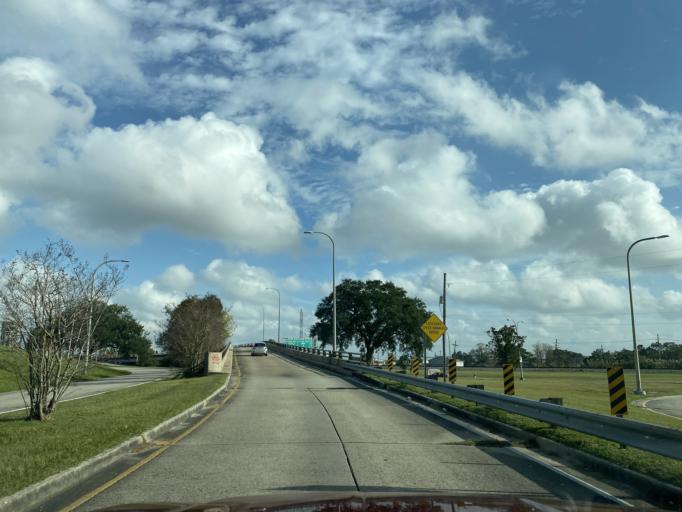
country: US
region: Louisiana
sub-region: Orleans Parish
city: New Orleans
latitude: 30.0312
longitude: -90.0401
